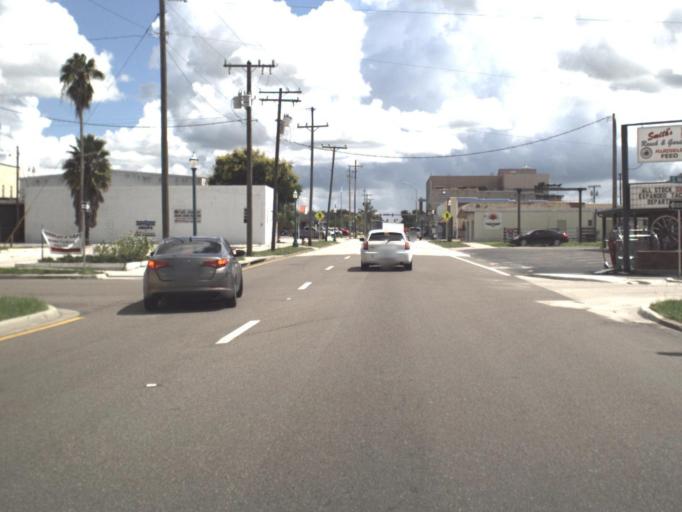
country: US
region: Florida
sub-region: DeSoto County
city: Arcadia
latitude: 27.2153
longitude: -81.8633
